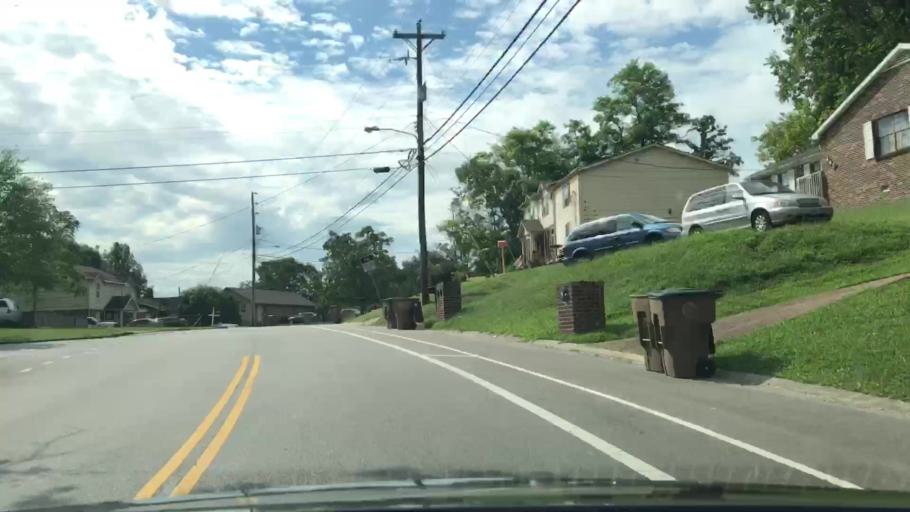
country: US
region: Tennessee
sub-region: Williamson County
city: Brentwood Estates
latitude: 36.0378
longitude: -86.7064
